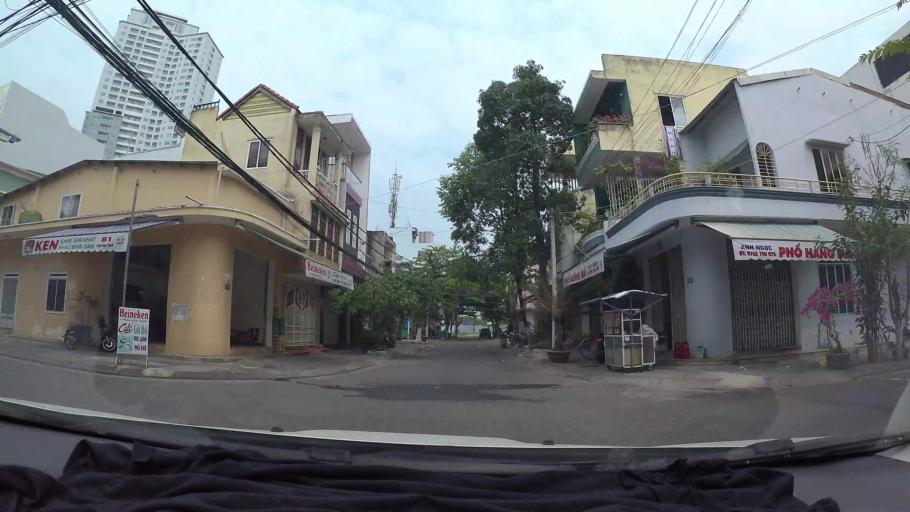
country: VN
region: Da Nang
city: Da Nang
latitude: 16.0893
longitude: 108.2170
